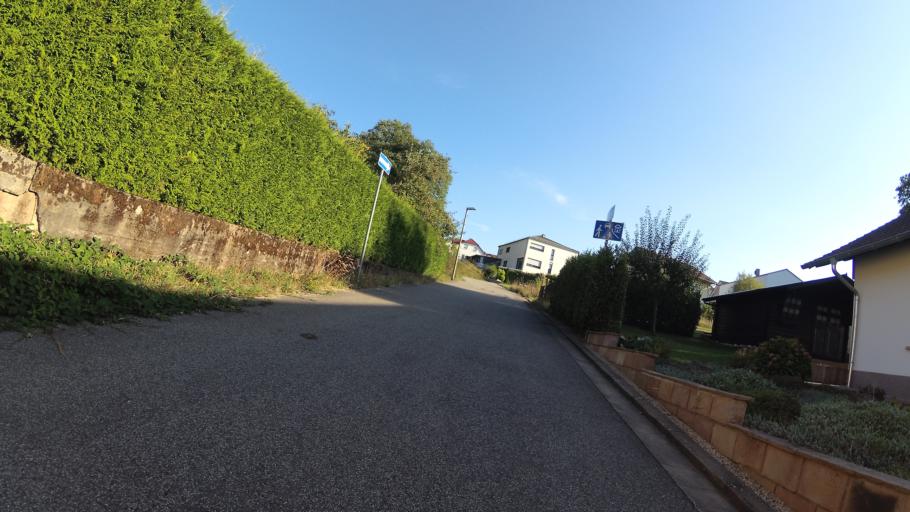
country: DE
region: Saarland
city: Eppelborn
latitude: 49.4107
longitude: 6.9801
